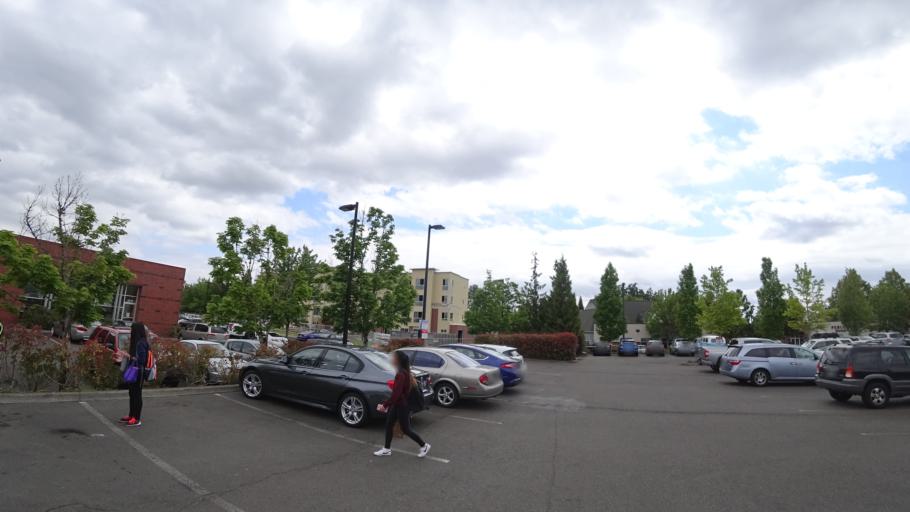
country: US
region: Oregon
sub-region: Washington County
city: Rockcreek
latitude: 45.5361
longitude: -122.8834
